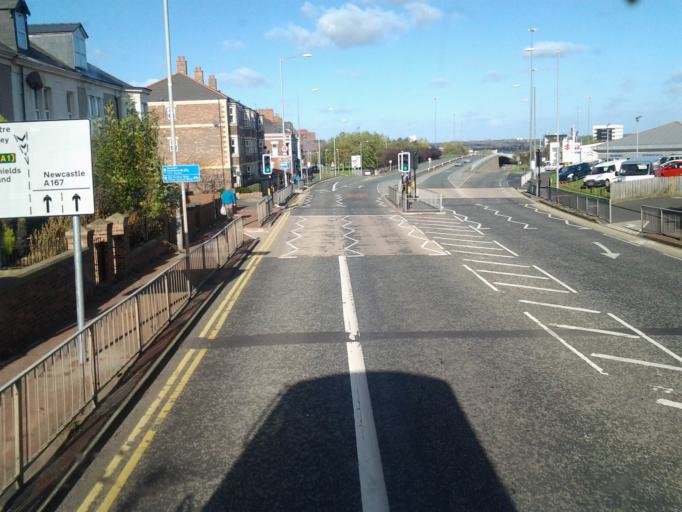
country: GB
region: England
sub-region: Gateshead
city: Gateshead
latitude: 54.9538
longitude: -1.5998
